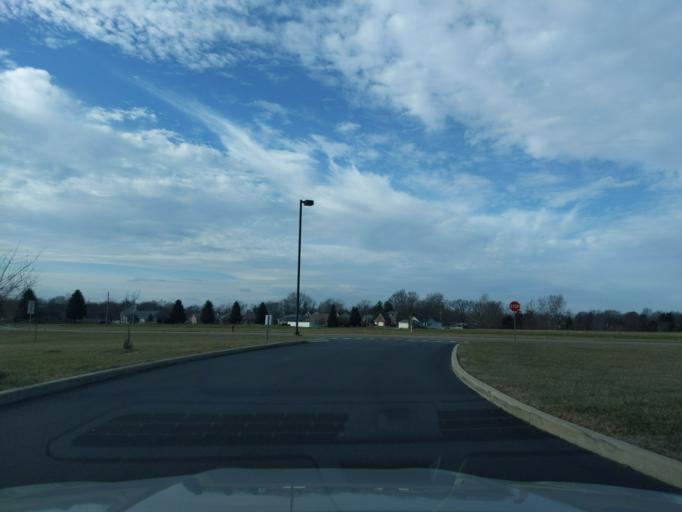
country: US
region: Indiana
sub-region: Decatur County
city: Greensburg
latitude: 39.3200
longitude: -85.4676
